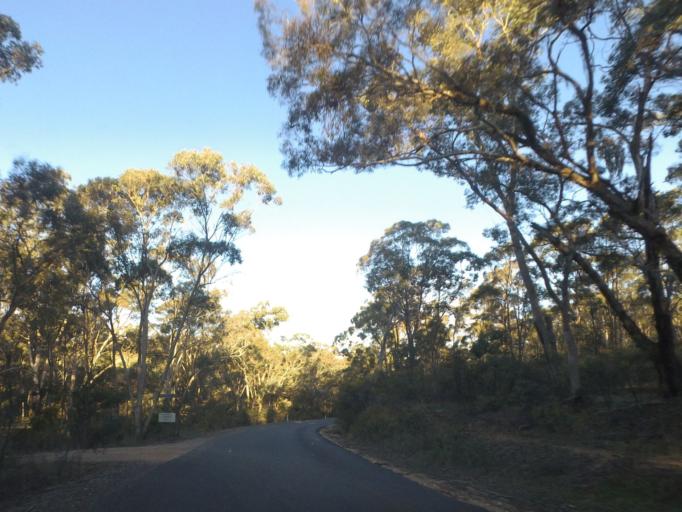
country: AU
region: Victoria
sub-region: Mount Alexander
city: Castlemaine
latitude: -37.1486
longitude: 144.2056
